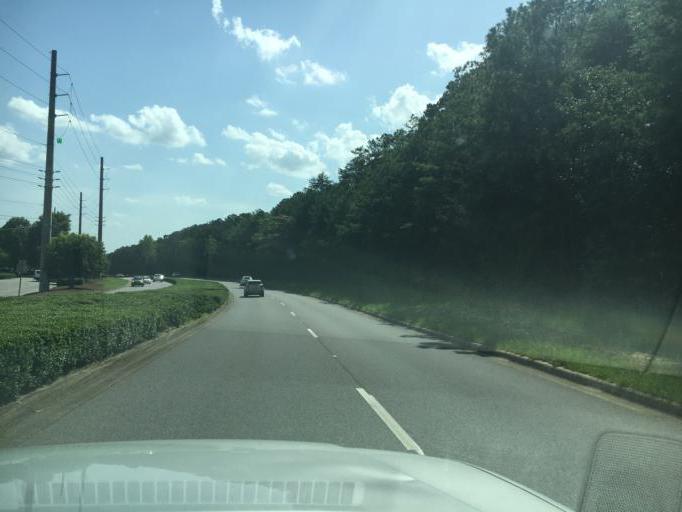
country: US
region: Alabama
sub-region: Shelby County
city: Meadowbrook
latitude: 33.4180
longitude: -86.6966
